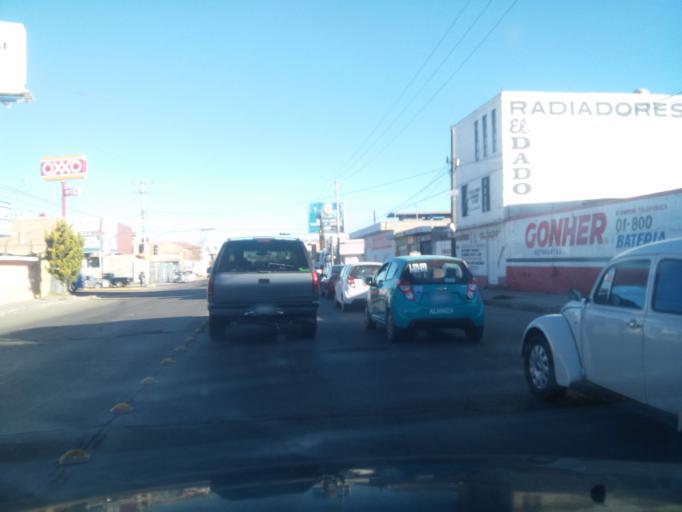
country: MX
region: Durango
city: Victoria de Durango
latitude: 24.0128
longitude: -104.6447
